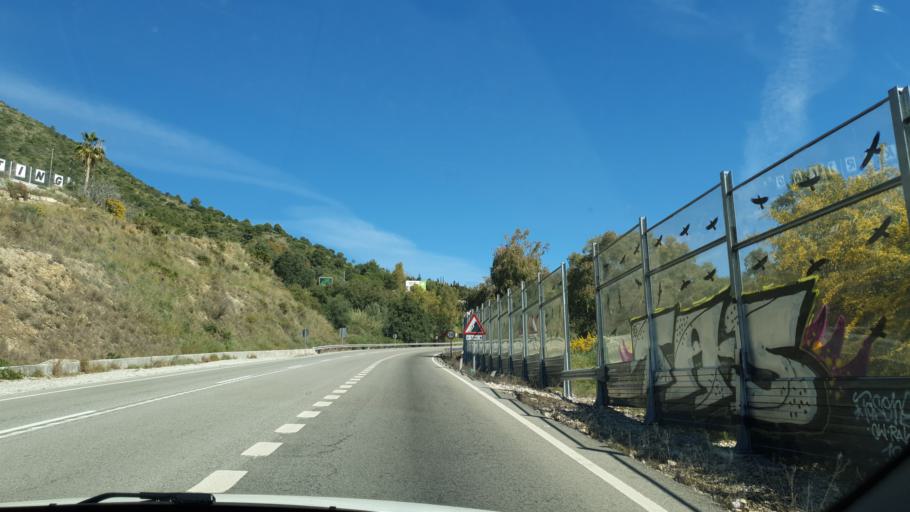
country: ES
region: Andalusia
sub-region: Provincia de Malaga
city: Ojen
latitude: 36.5420
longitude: -4.8644
